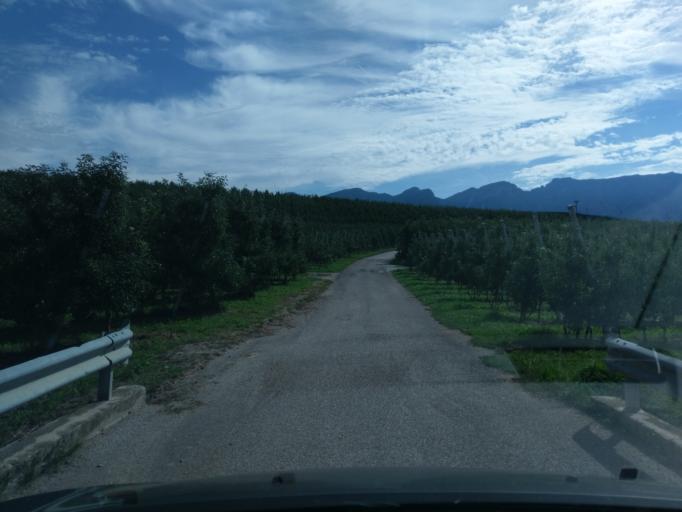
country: IT
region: Trentino-Alto Adige
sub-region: Provincia di Trento
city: Flavon
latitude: 46.2955
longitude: 11.0376
